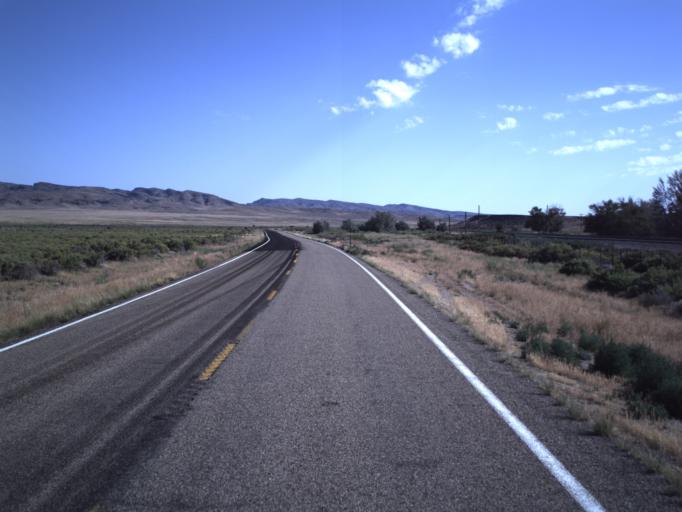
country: US
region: Utah
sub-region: Beaver County
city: Milford
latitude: 38.7126
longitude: -112.9693
